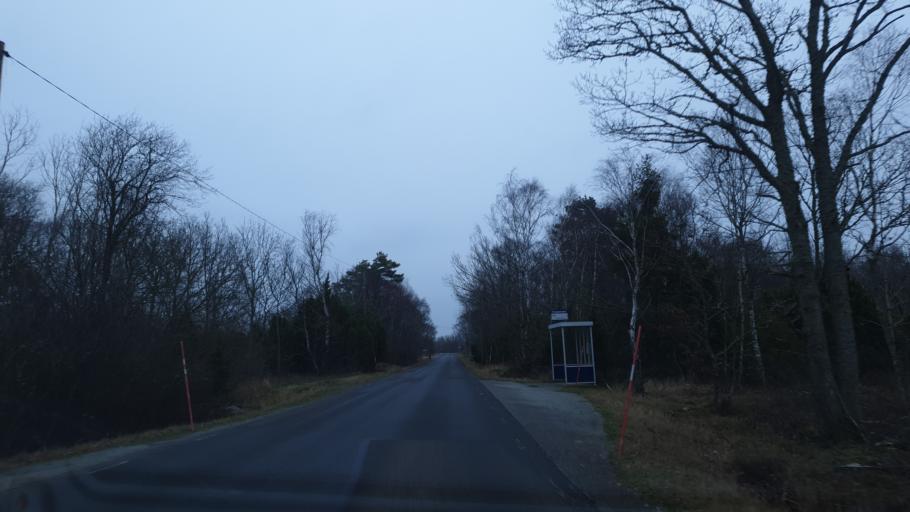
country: SE
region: Blekinge
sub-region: Karlskrona Kommun
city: Sturko
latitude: 56.1082
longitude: 15.6448
